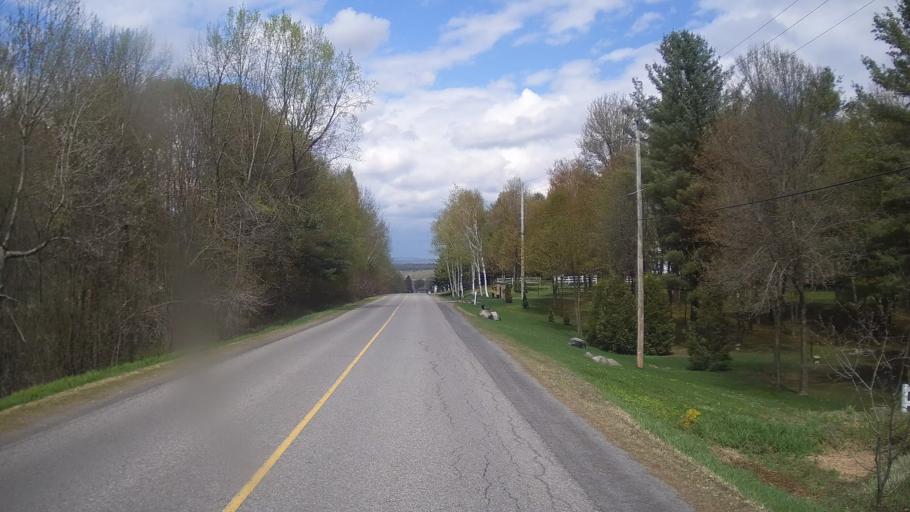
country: CA
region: Ontario
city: Hawkesbury
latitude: 45.5785
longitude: -74.5207
